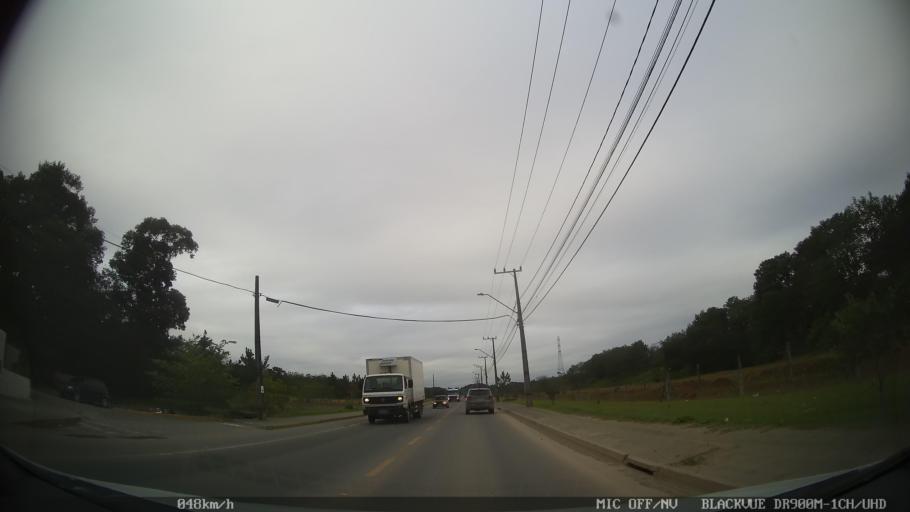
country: BR
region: Santa Catarina
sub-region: Joinville
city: Joinville
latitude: -26.3375
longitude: -48.8945
